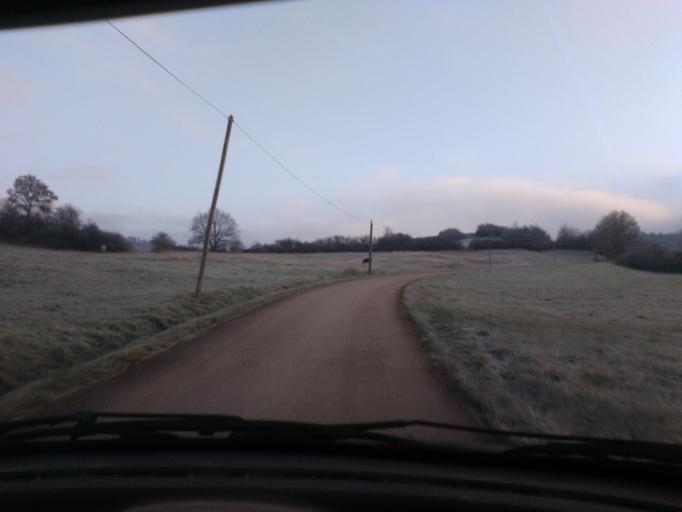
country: FR
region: Lorraine
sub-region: Departement des Vosges
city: Saint-Die-des-Vosges
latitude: 48.3087
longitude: 6.9640
